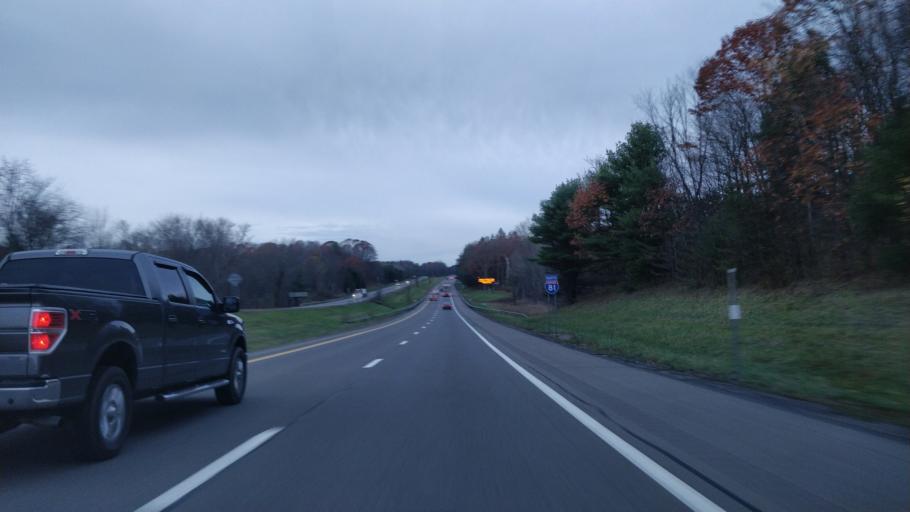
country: US
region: New York
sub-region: Oswego County
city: Central Square
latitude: 43.3749
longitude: -76.1219
